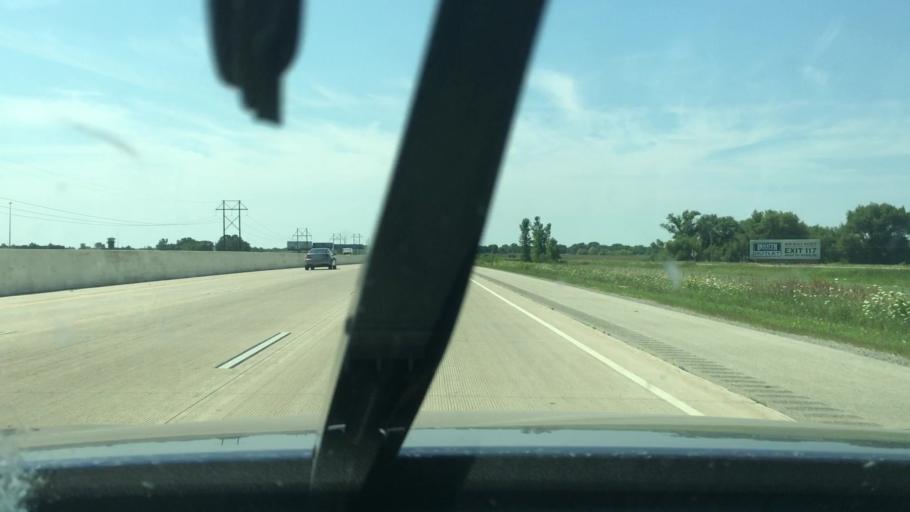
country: US
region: Wisconsin
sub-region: Winnebago County
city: Oshkosh
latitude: 44.0807
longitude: -88.5621
